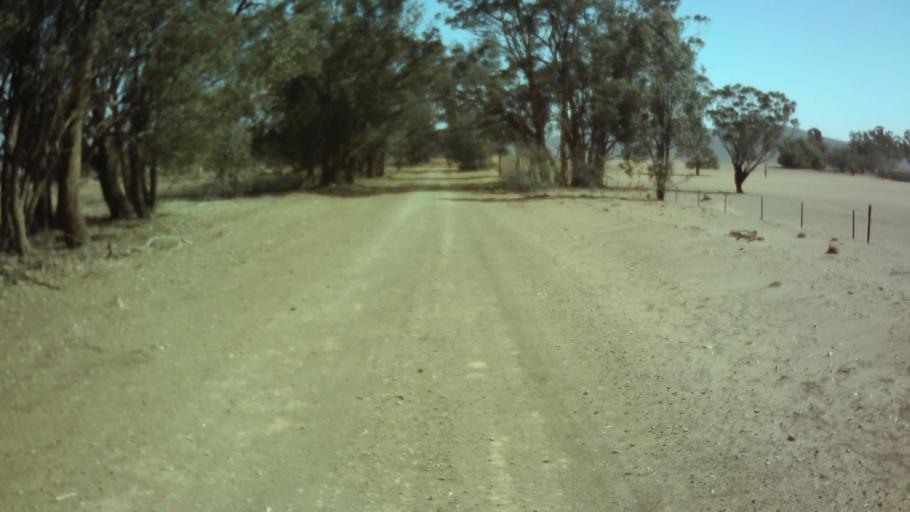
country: AU
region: New South Wales
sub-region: Weddin
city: Grenfell
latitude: -33.8439
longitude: 148.0176
